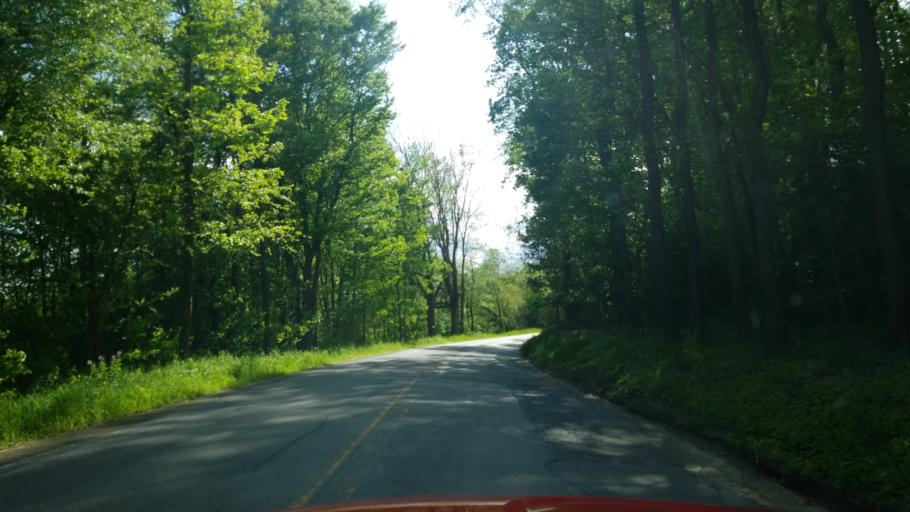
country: US
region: Pennsylvania
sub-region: Clearfield County
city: Hyde
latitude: 40.9771
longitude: -78.4756
